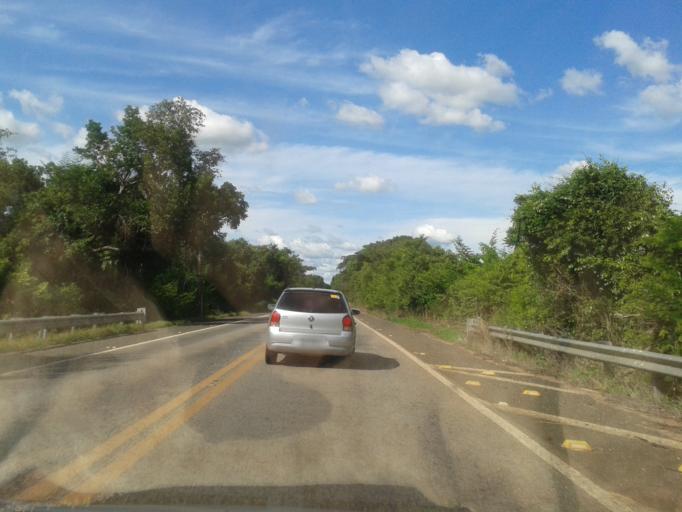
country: BR
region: Goias
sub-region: Mozarlandia
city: Mozarlandia
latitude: -15.0000
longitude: -50.5889
